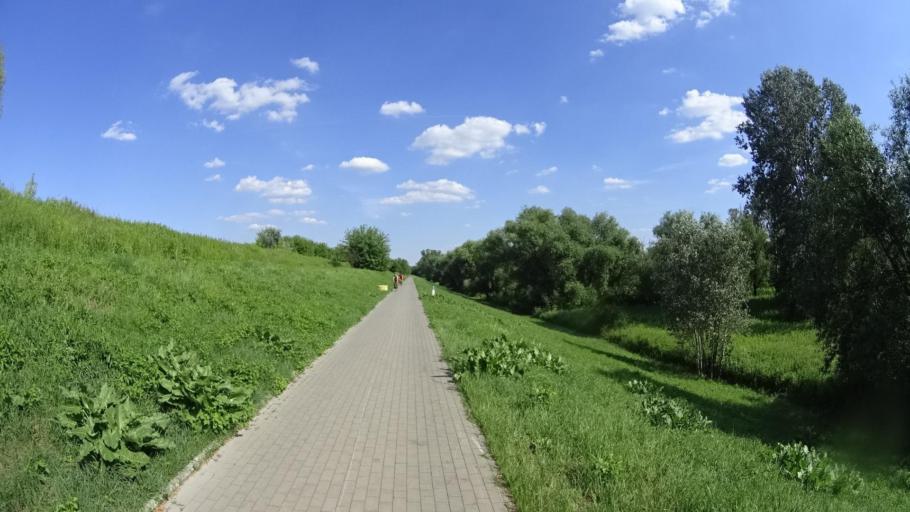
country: PL
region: Masovian Voivodeship
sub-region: Warszawa
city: Bialoleka
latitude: 52.3031
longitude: 20.9649
